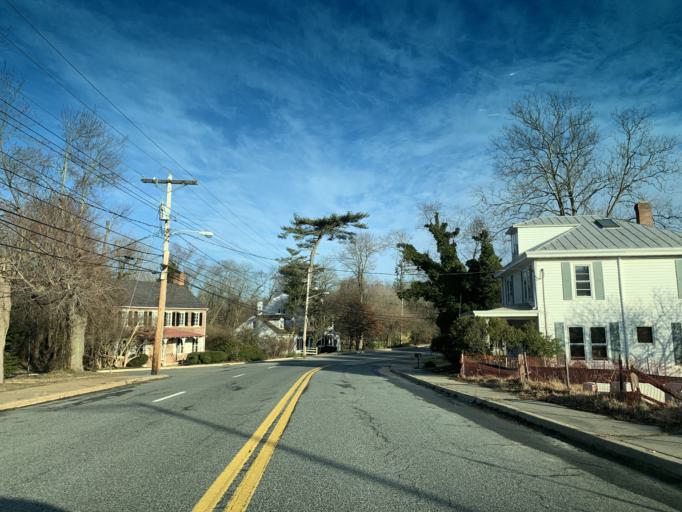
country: US
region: Delaware
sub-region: New Castle County
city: Bear
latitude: 39.6650
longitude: -75.6588
